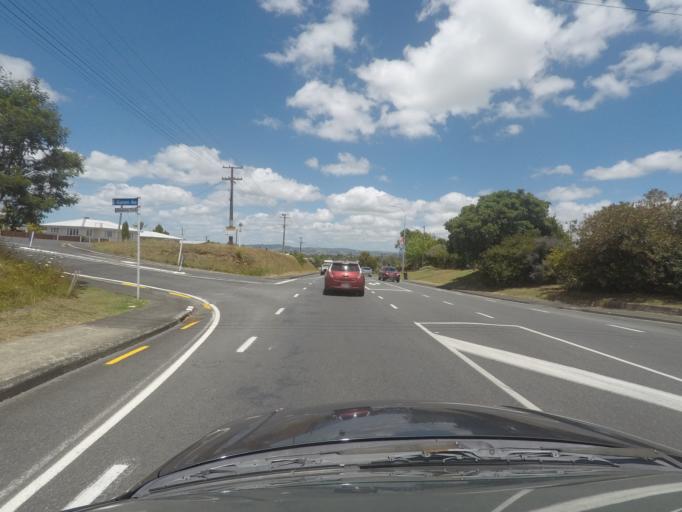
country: NZ
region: Northland
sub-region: Whangarei
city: Whangarei
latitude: -35.7504
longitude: 174.3678
